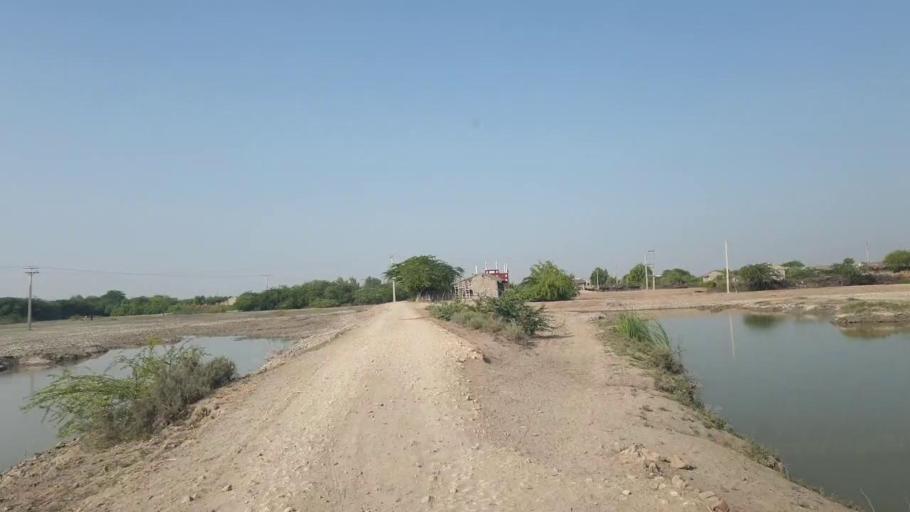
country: PK
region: Sindh
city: Badin
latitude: 24.5219
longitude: 68.7641
